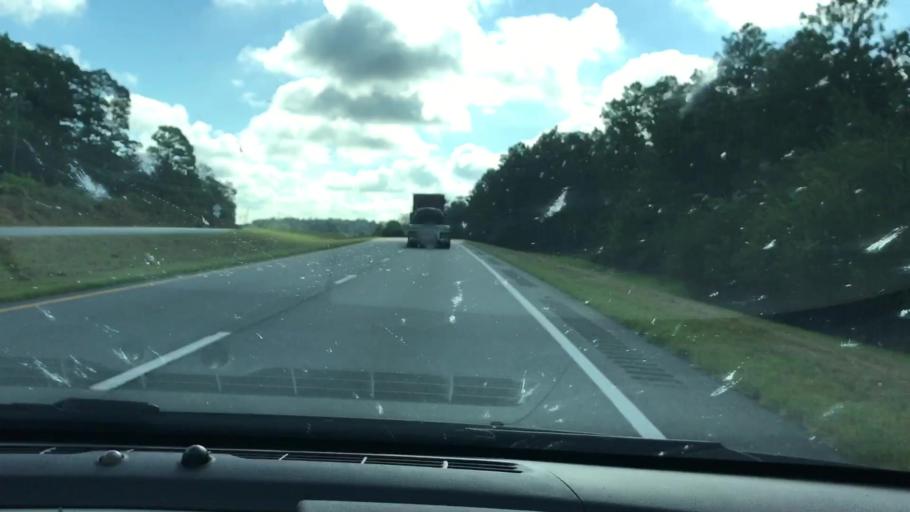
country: US
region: Georgia
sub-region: Worth County
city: Sylvester
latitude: 31.5502
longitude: -83.9669
